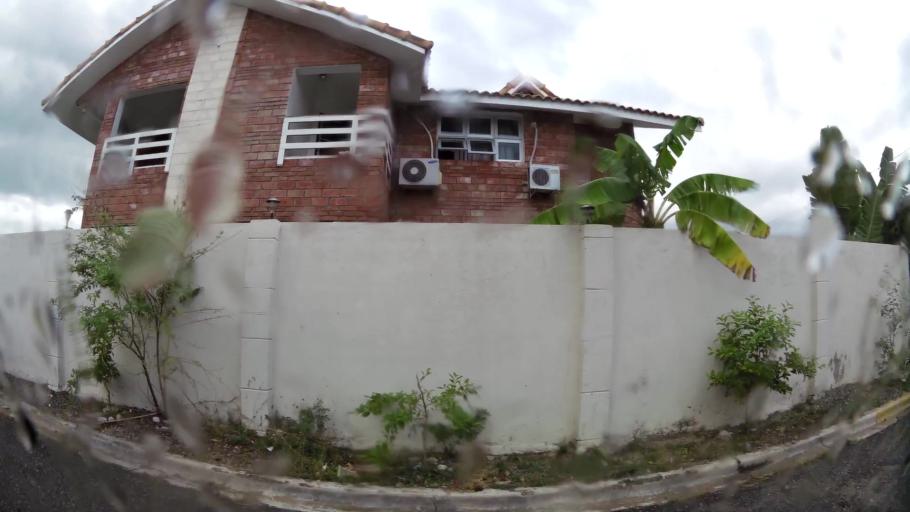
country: DO
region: Nacional
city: La Agustina
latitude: 18.5101
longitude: -69.9389
